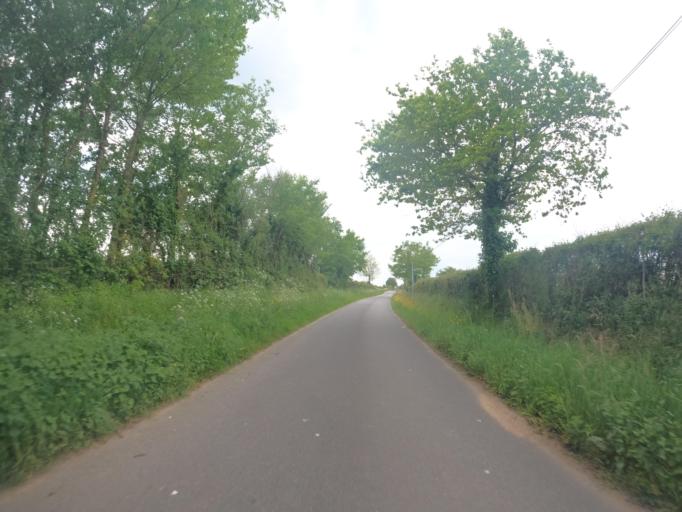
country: FR
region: Poitou-Charentes
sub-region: Departement des Deux-Sevres
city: Saint-Varent
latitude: 46.8672
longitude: -0.3063
